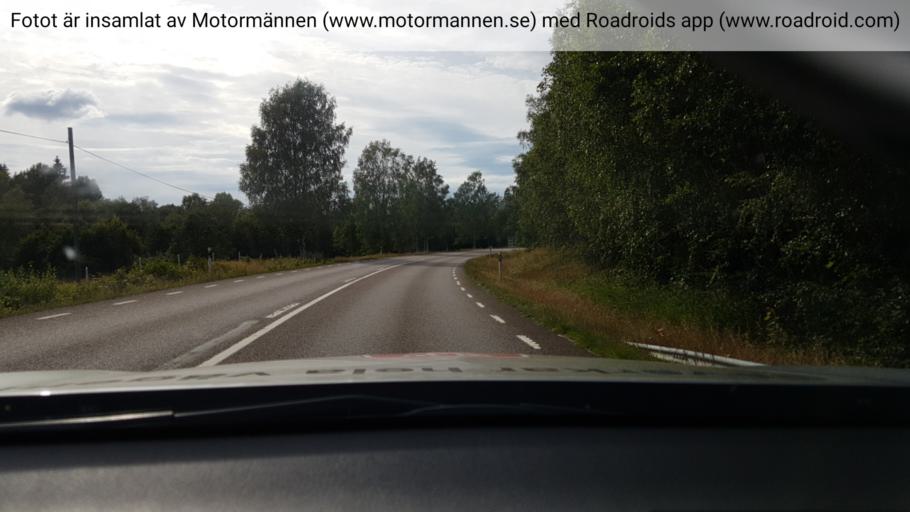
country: SE
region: Vaestra Goetaland
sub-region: Amals Kommun
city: Amal
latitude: 59.0719
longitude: 12.6408
